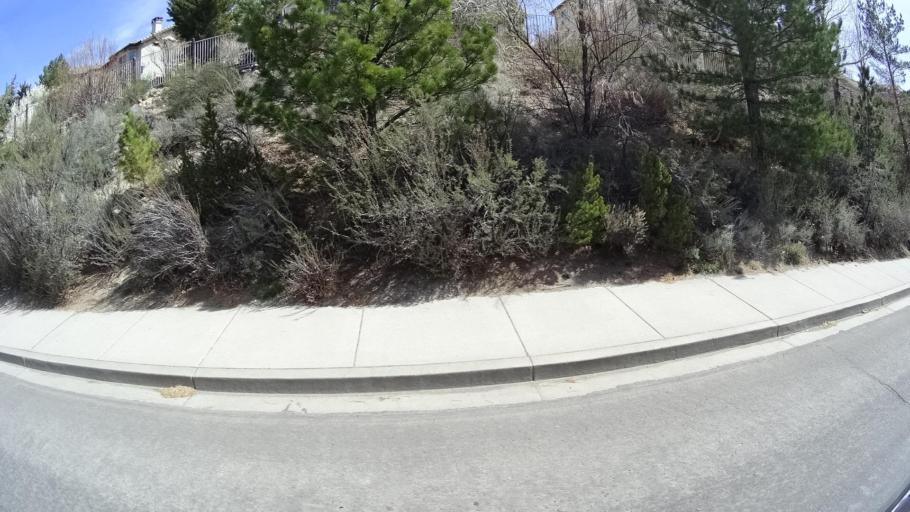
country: US
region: Nevada
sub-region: Washoe County
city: Reno
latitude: 39.4843
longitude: -119.8606
